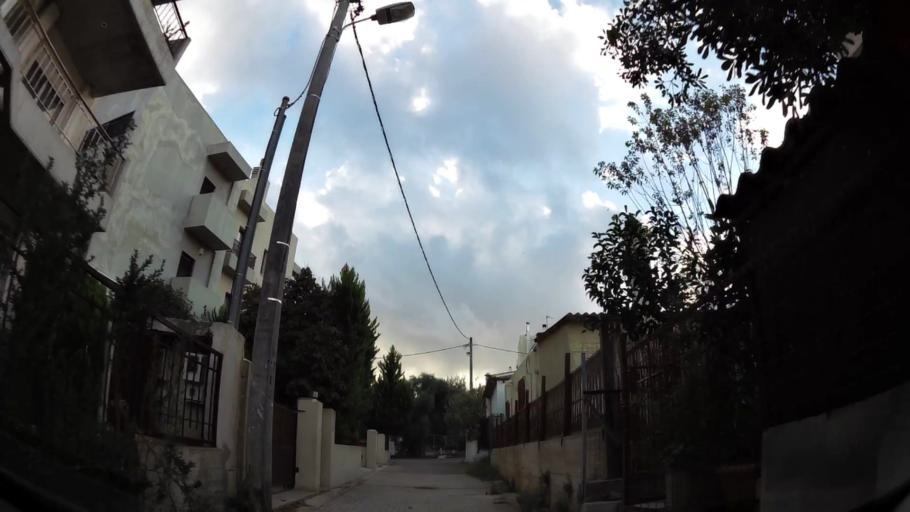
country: GR
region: Attica
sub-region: Nomarchia Athinas
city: Marousi
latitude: 38.0458
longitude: 23.8117
